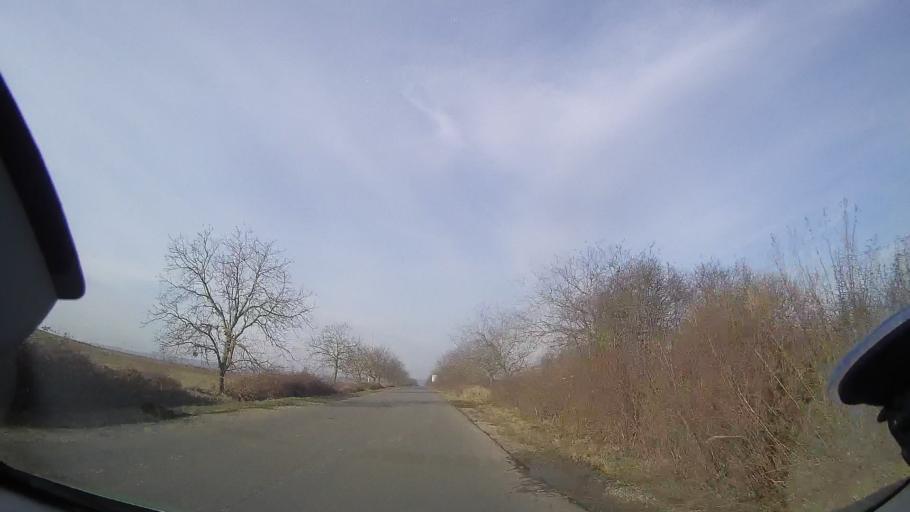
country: RO
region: Bihor
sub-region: Comuna Spinus
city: Spinus
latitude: 47.2193
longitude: 22.1728
